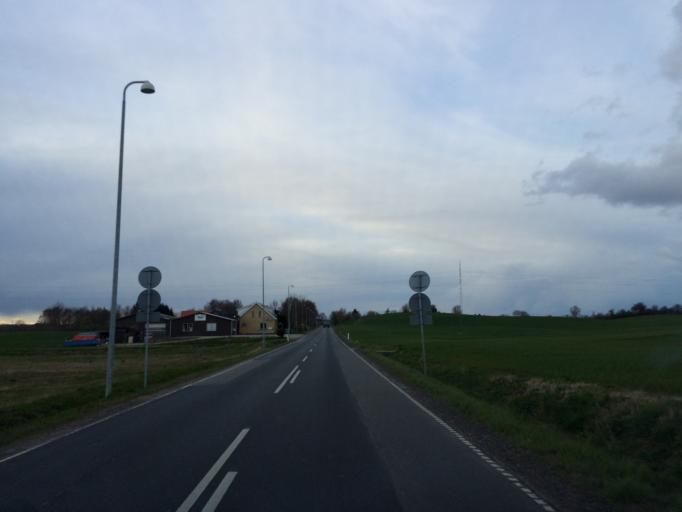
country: DK
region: South Denmark
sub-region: Odense Kommune
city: Bellinge
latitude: 55.3533
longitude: 10.2767
